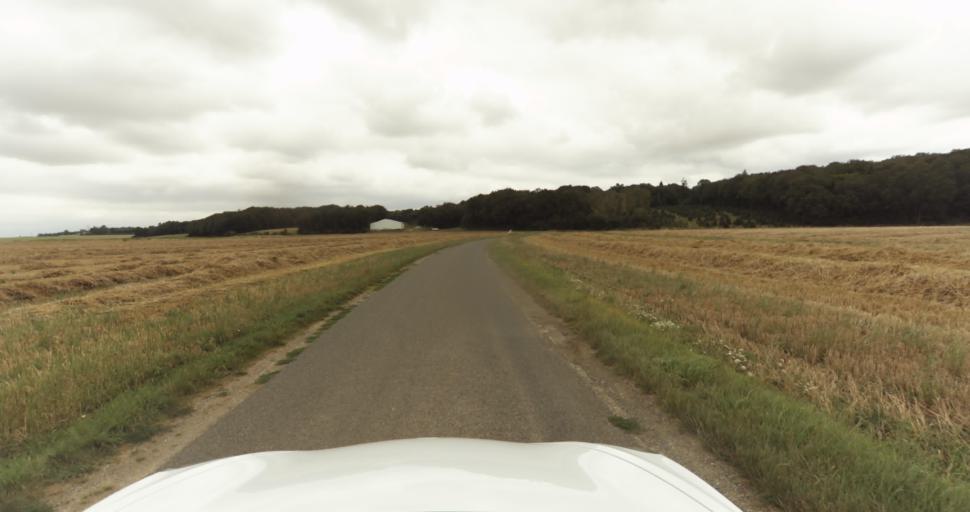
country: FR
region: Haute-Normandie
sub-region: Departement de l'Eure
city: Saint-Sebastien-de-Morsent
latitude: 49.0282
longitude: 1.0615
